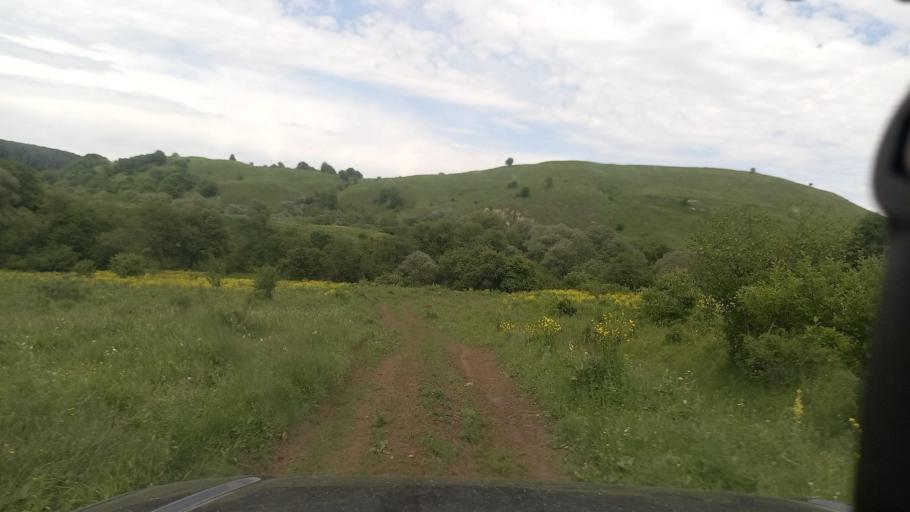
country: RU
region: Karachayevo-Cherkesiya
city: Pregradnaya
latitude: 44.0770
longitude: 41.2729
